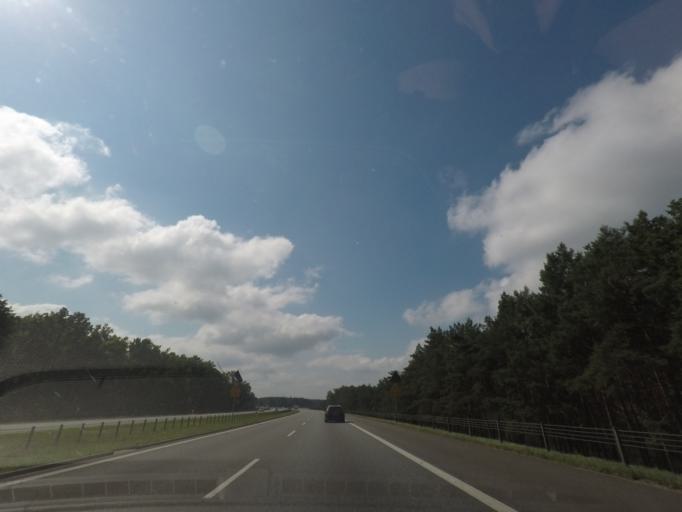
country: PL
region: Kujawsko-Pomorskie
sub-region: Powiat torunski
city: Lubicz Dolny
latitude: 53.0048
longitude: 18.7327
